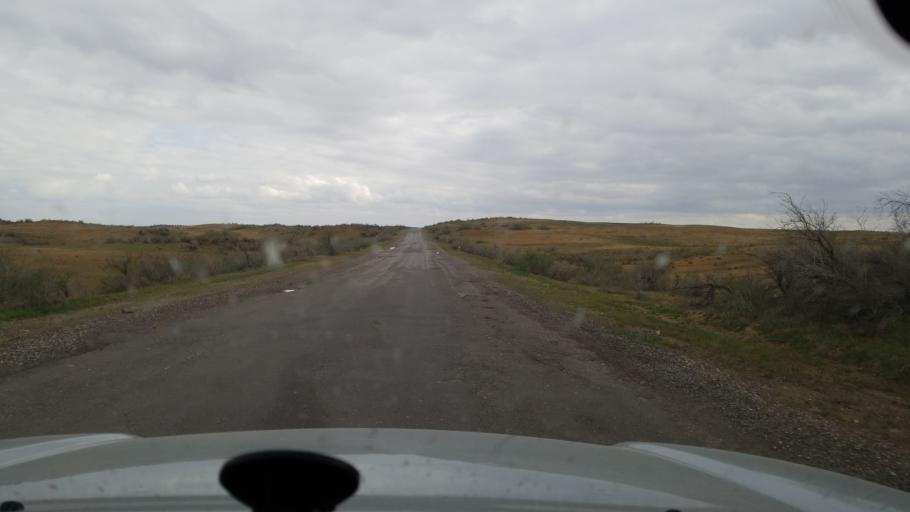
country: TM
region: Mary
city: Serhetabat
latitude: 36.0855
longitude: 62.6134
